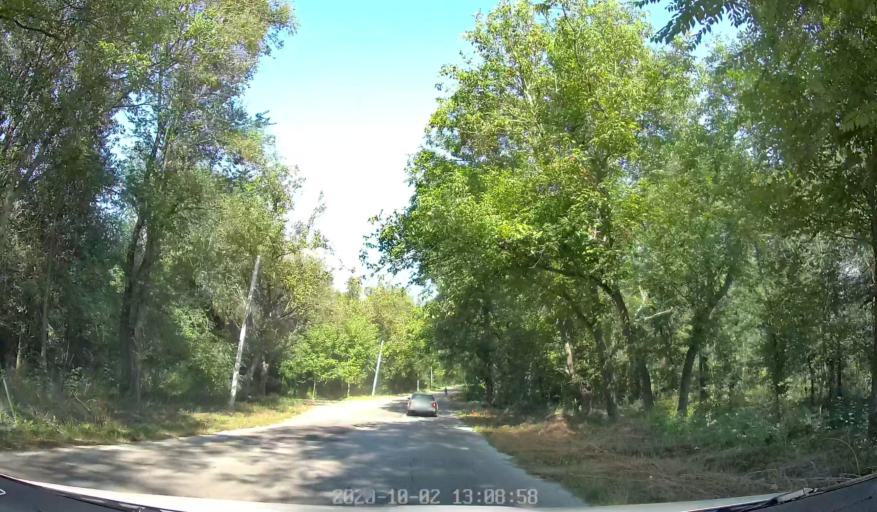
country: MD
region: Chisinau
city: Singera
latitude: 46.9458
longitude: 28.9297
